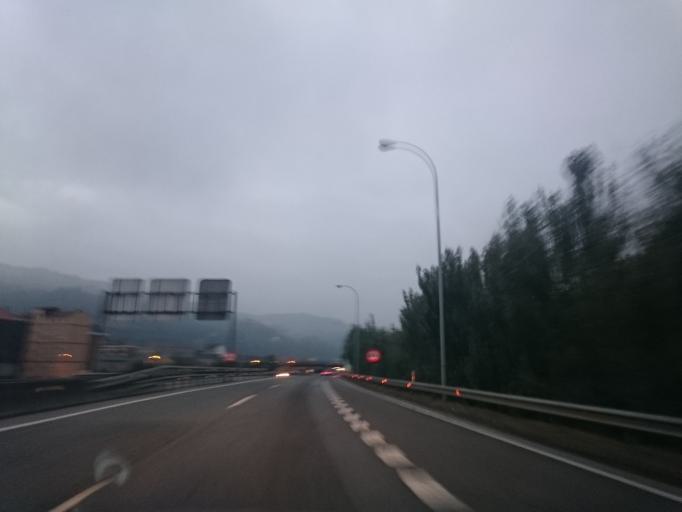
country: ES
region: Asturias
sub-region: Province of Asturias
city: Mieres
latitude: 43.2520
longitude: -5.7812
